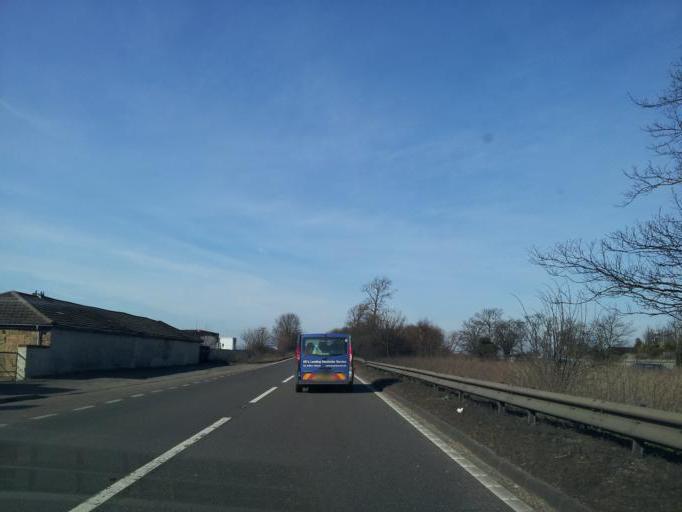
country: GB
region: England
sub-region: Peterborough
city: Castor
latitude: 52.5473
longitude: -0.3342
